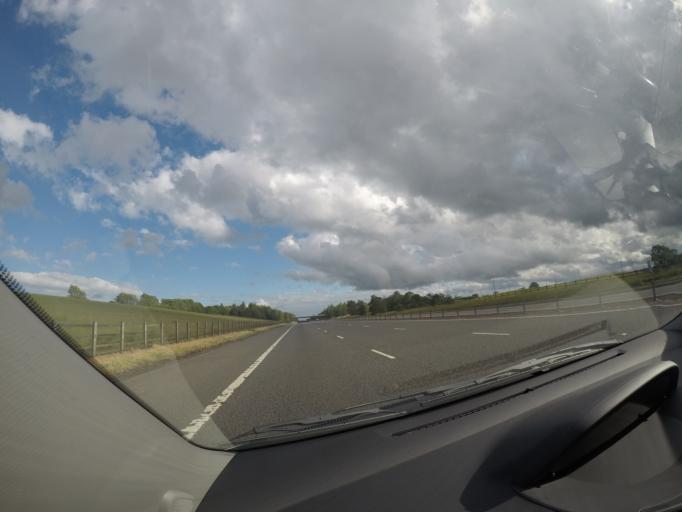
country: GB
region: Scotland
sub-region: Dumfries and Galloway
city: Lockerbie
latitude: 55.1274
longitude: -3.3657
